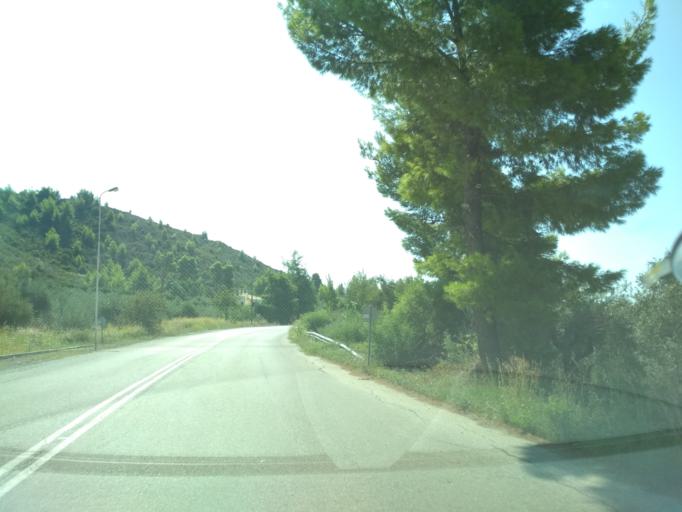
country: GR
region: Central Greece
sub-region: Nomos Evvoias
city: Roviai
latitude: 38.8215
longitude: 23.2290
